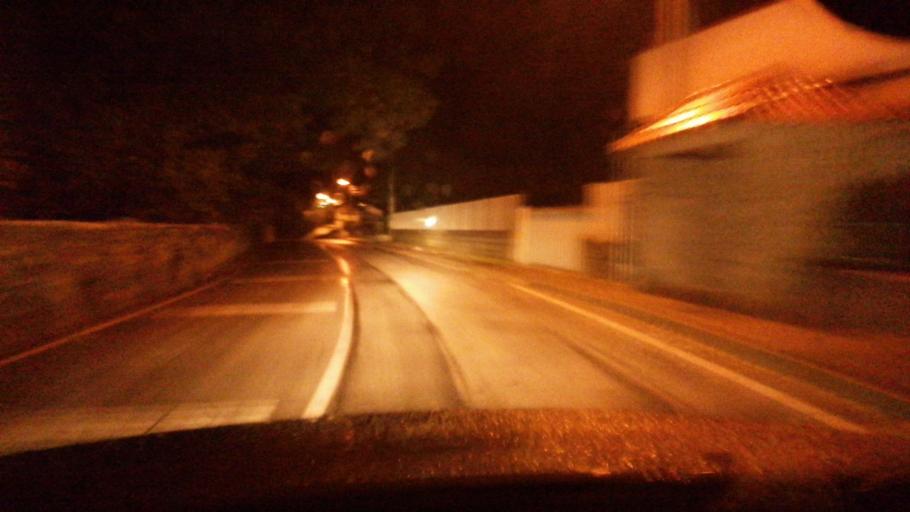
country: PT
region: Viseu
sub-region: Armamar
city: Armamar
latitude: 41.0808
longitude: -7.6716
